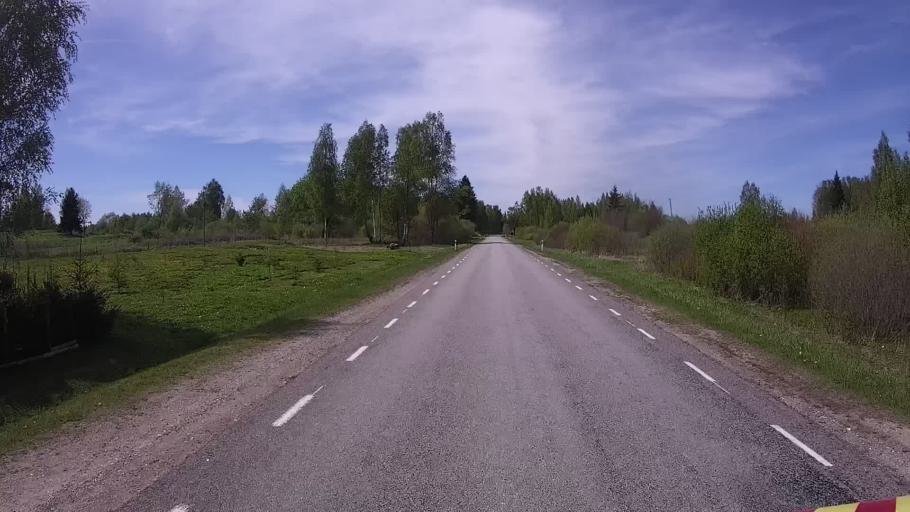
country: EE
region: Valgamaa
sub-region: Valga linn
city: Valga
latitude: 57.6454
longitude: 26.3211
